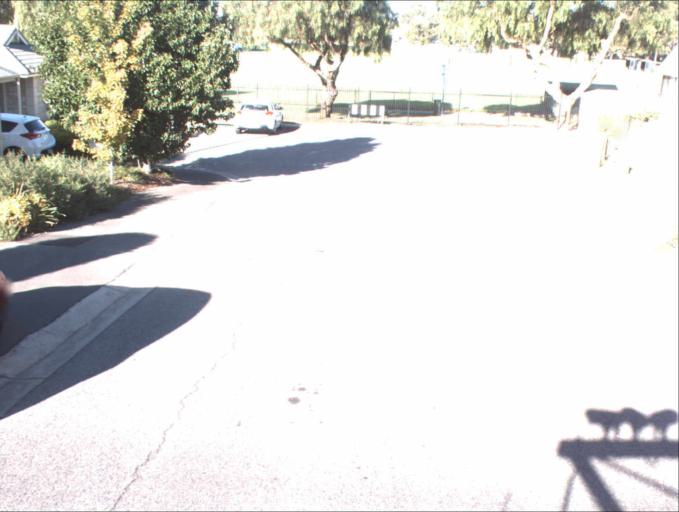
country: AU
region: South Australia
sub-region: Port Adelaide Enfield
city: Klemzig
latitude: -34.8749
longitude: 138.6453
